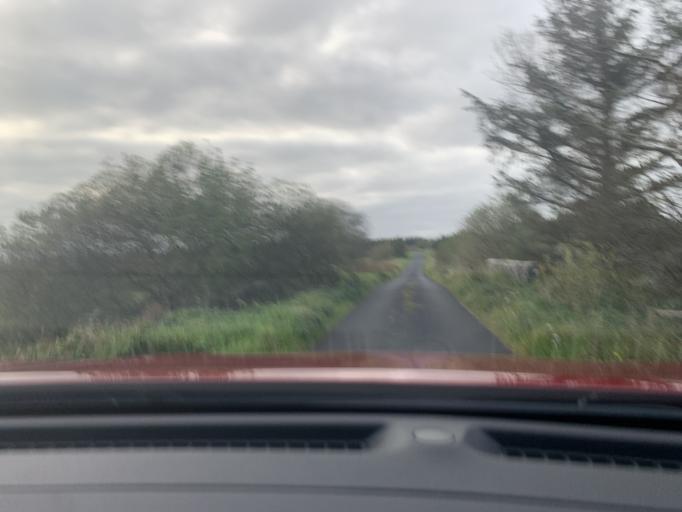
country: IE
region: Connaught
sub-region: Sligo
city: Tobercurry
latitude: 54.0176
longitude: -8.6260
